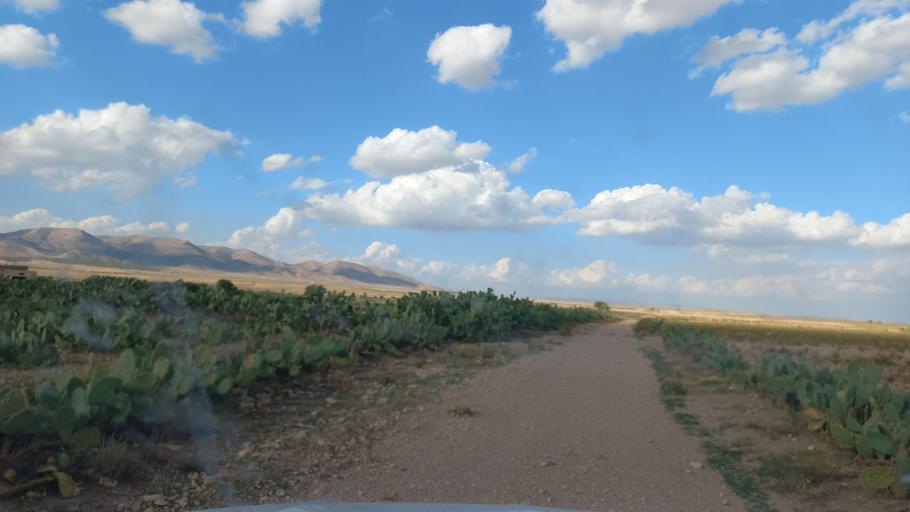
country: TN
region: Al Qasrayn
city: Sbiba
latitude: 35.3910
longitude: 9.0433
